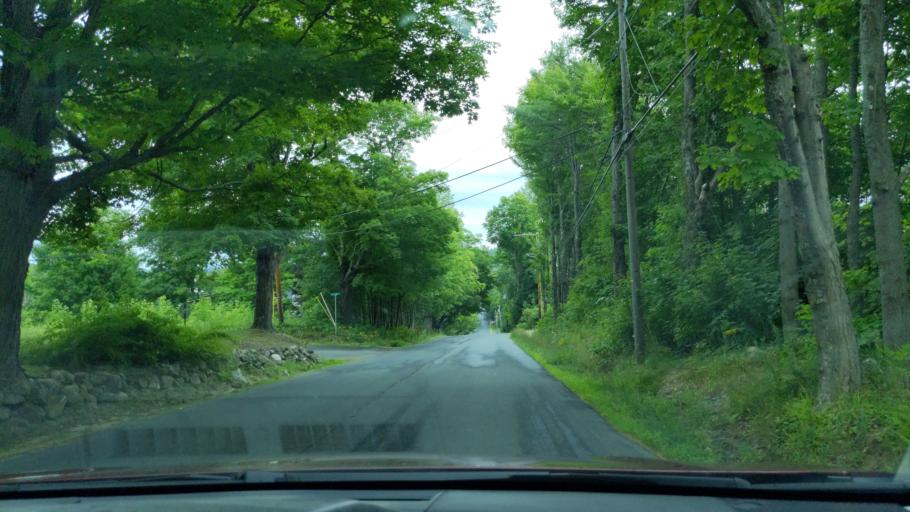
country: US
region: New Hampshire
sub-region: Merrimack County
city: New London
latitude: 43.4182
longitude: -72.0198
